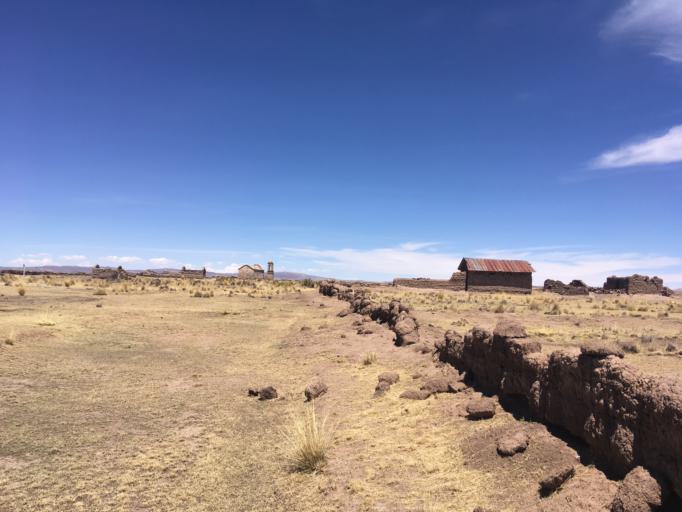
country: PE
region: Puno
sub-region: Provincia de Chucuito
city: Kelluyo
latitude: -17.0616
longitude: -69.1811
